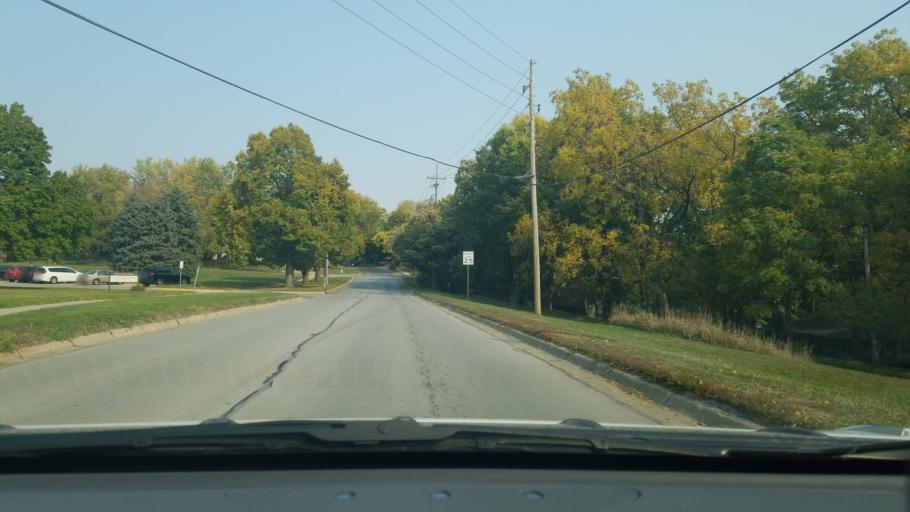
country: US
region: Nebraska
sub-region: Sarpy County
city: Bellevue
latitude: 41.1587
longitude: -95.9091
